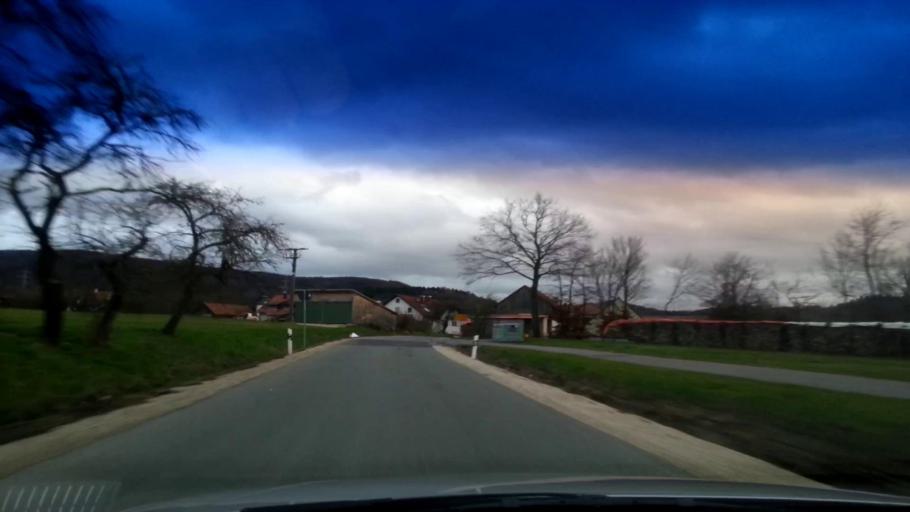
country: DE
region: Bavaria
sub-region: Upper Franconia
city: Schesslitz
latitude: 49.9732
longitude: 11.0579
